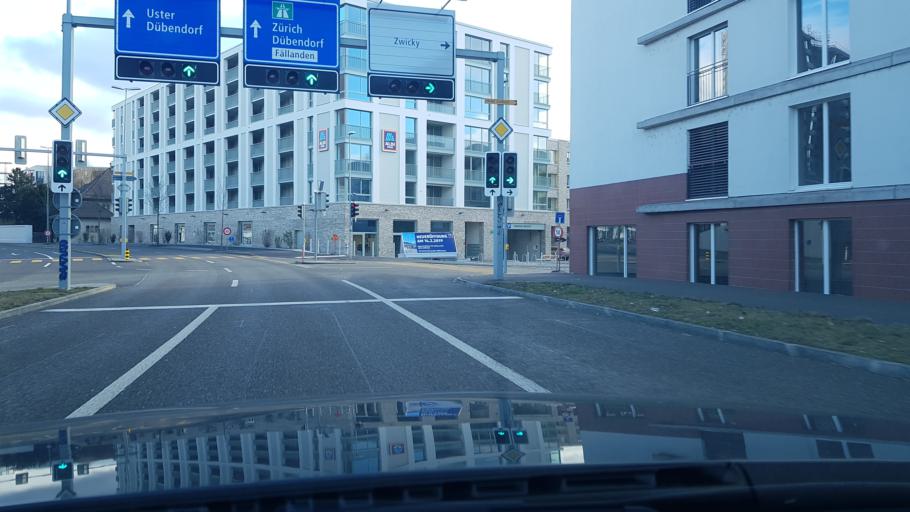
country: CH
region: Zurich
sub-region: Bezirk Buelach
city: Wallisellen / Wallisellen-Ost
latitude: 47.4058
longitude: 8.6022
